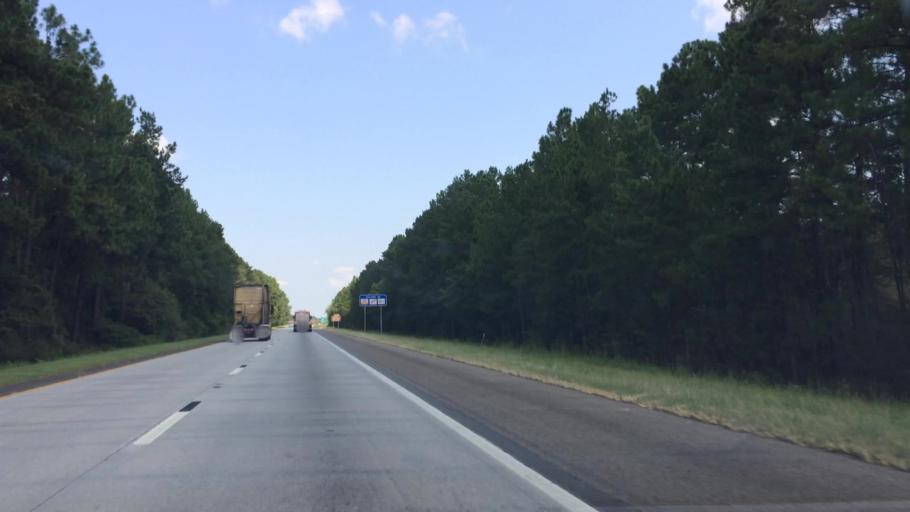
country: US
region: South Carolina
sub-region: Dorchester County
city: Saint George
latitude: 33.0724
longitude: -80.6581
